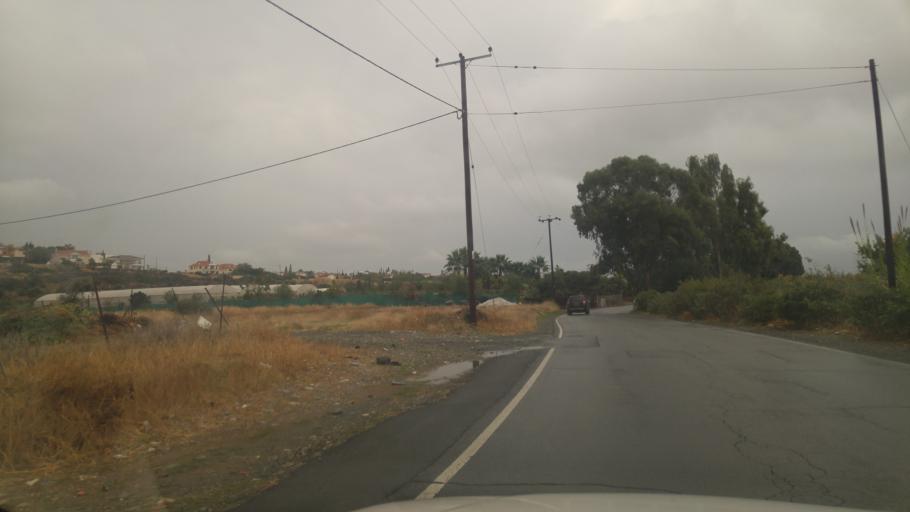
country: CY
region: Limassol
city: Mouttagiaka
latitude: 34.7140
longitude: 33.0890
